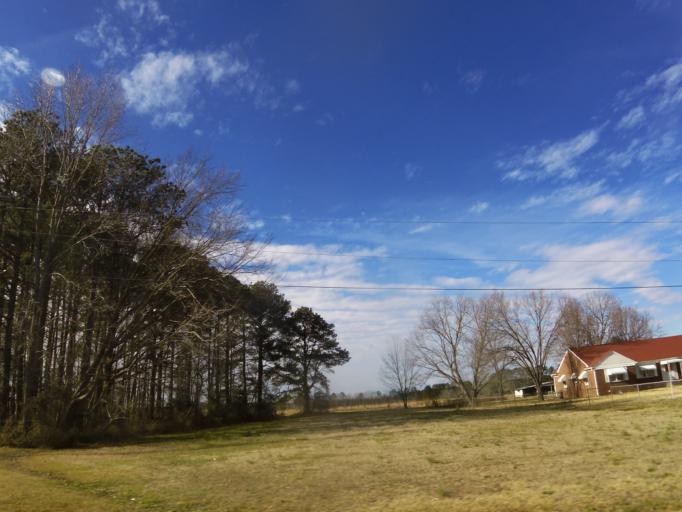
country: US
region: Virginia
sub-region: City of Franklin
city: Franklin
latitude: 36.6996
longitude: -76.8921
